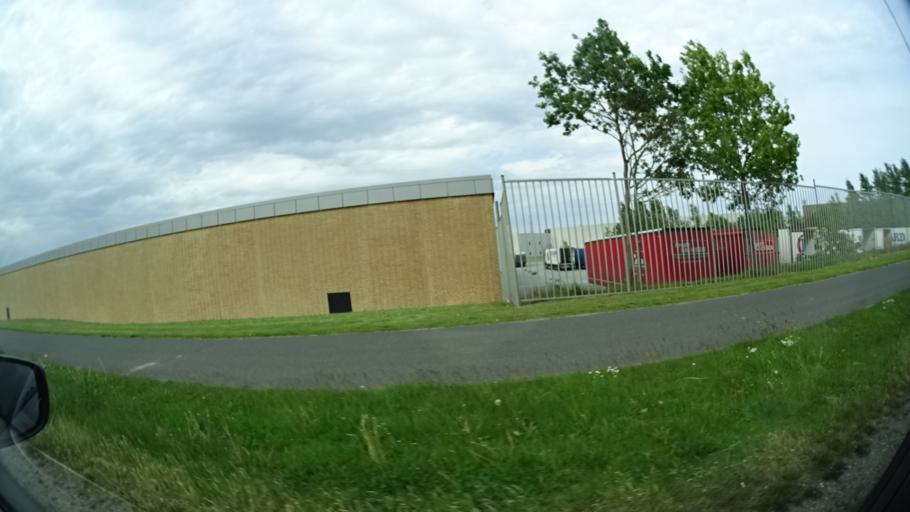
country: DK
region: Central Jutland
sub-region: Arhus Kommune
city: Marslet
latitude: 56.1103
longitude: 10.1617
